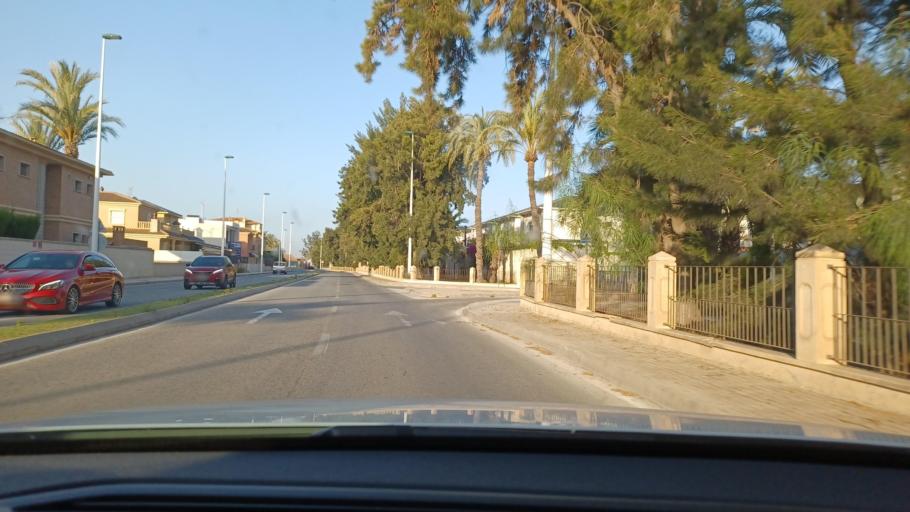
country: ES
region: Valencia
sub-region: Provincia de Alicante
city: Elche
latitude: 38.2566
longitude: -0.6878
